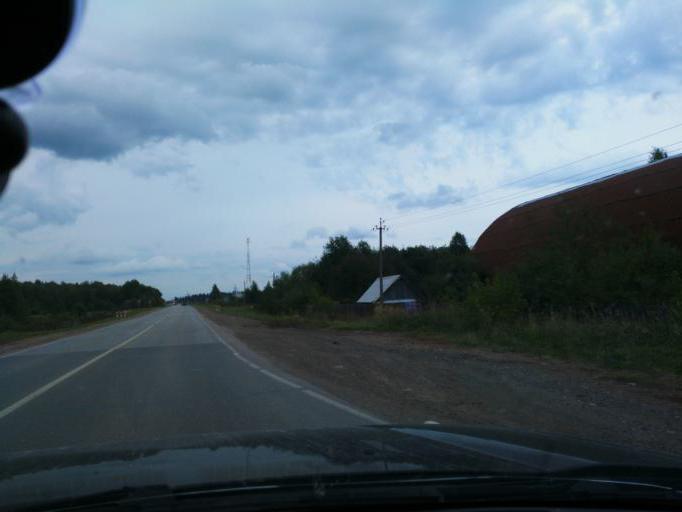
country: RU
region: Perm
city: Chernushka
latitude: 56.5335
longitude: 56.0689
